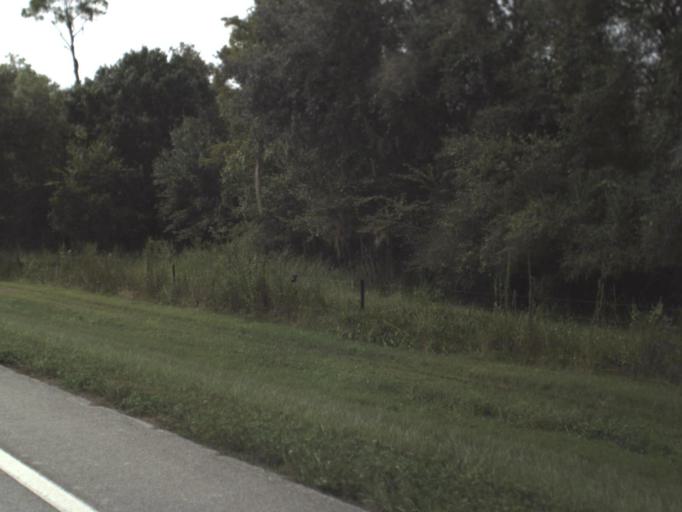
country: US
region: Florida
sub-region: DeSoto County
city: Nocatee
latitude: 27.2003
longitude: -81.9802
